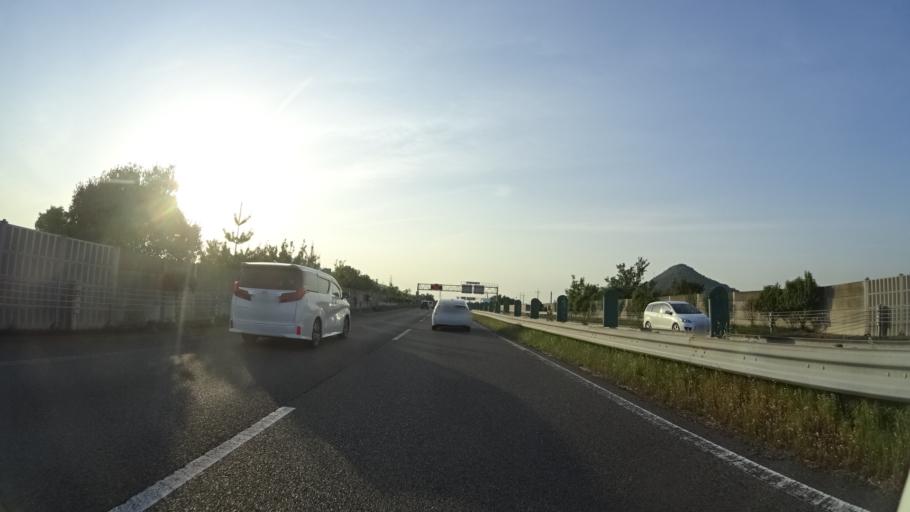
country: JP
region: Kagawa
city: Sakaidecho
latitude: 34.2911
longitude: 133.8490
